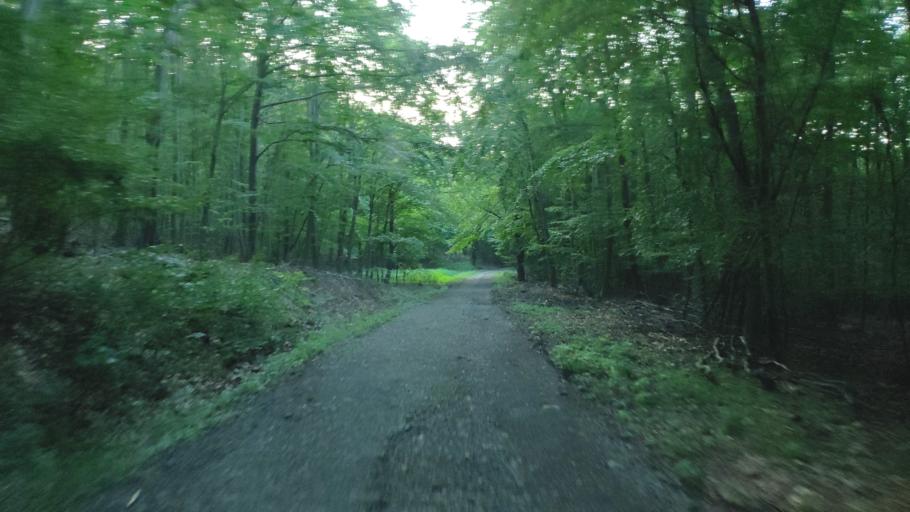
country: SK
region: Kosicky
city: Secovce
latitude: 48.5858
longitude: 21.5309
